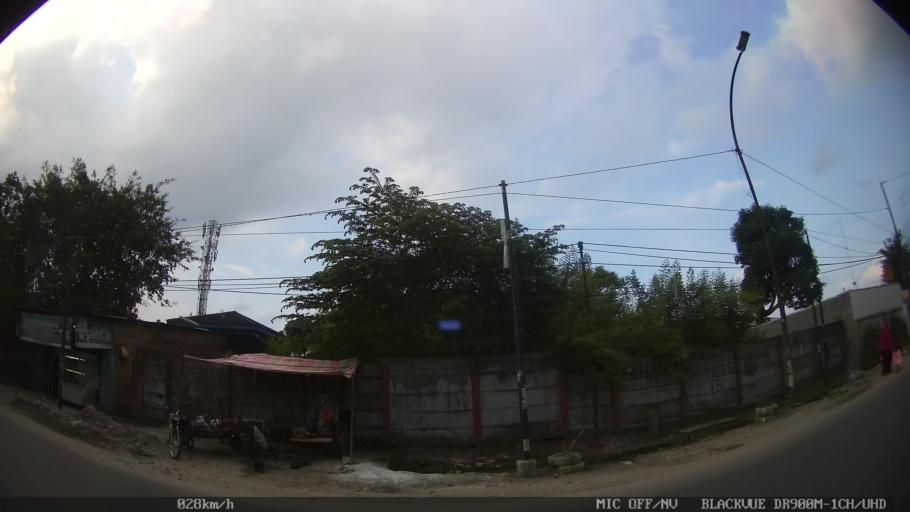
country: ID
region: North Sumatra
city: Medan
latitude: 3.5970
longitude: 98.7301
